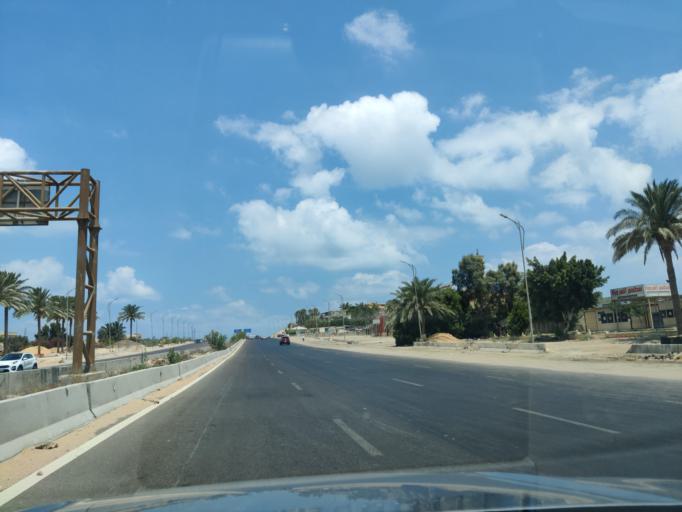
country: EG
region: Alexandria
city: Alexandria
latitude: 31.0086
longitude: 29.6378
